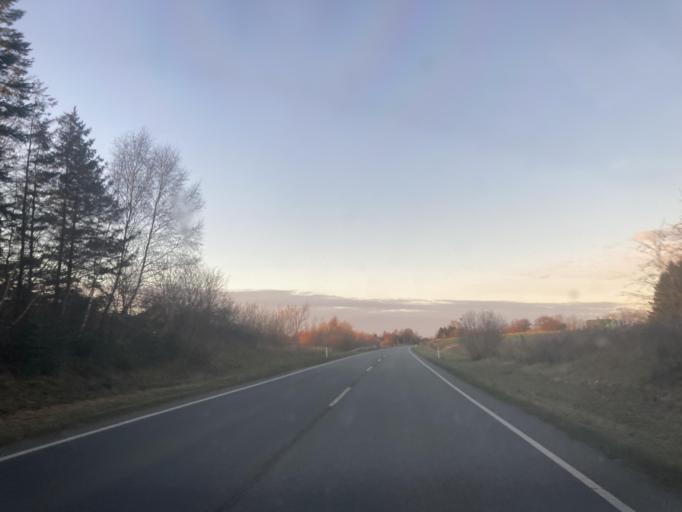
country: DK
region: Capital Region
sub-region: Gribskov Kommune
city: Graested
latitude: 56.0530
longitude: 12.2779
